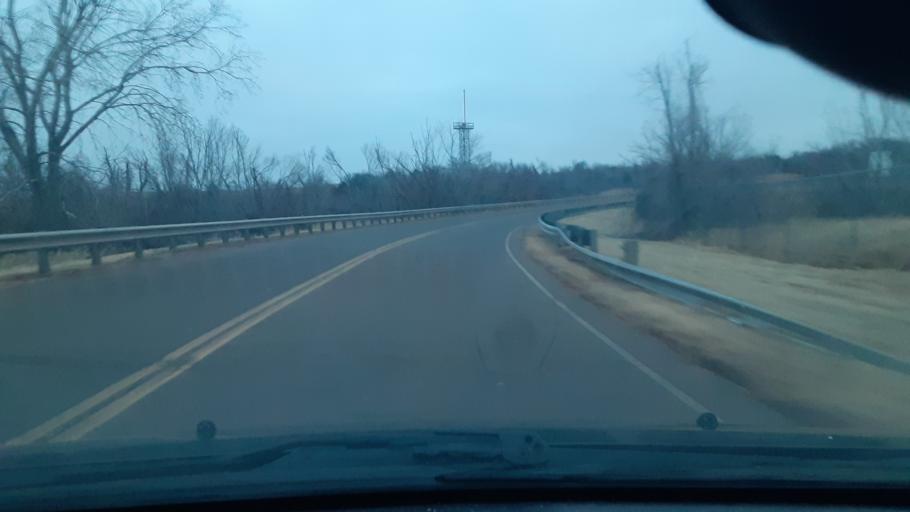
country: US
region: Oklahoma
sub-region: Logan County
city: Guthrie
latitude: 35.8610
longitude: -97.4204
